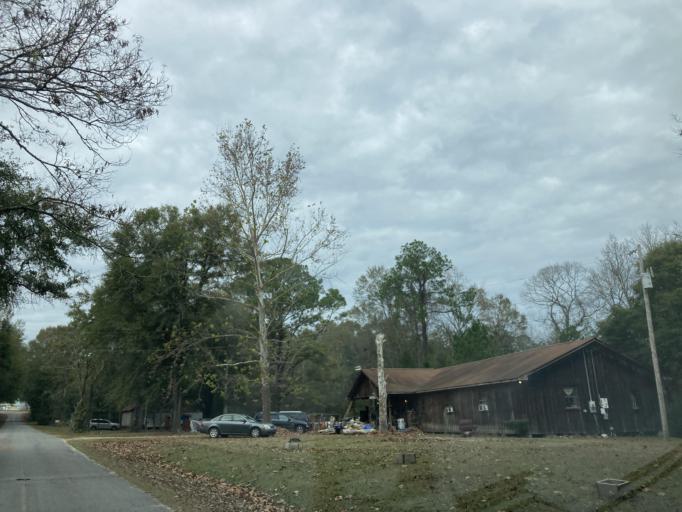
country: US
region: Mississippi
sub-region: Stone County
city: Wiggins
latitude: 31.0627
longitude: -89.2055
